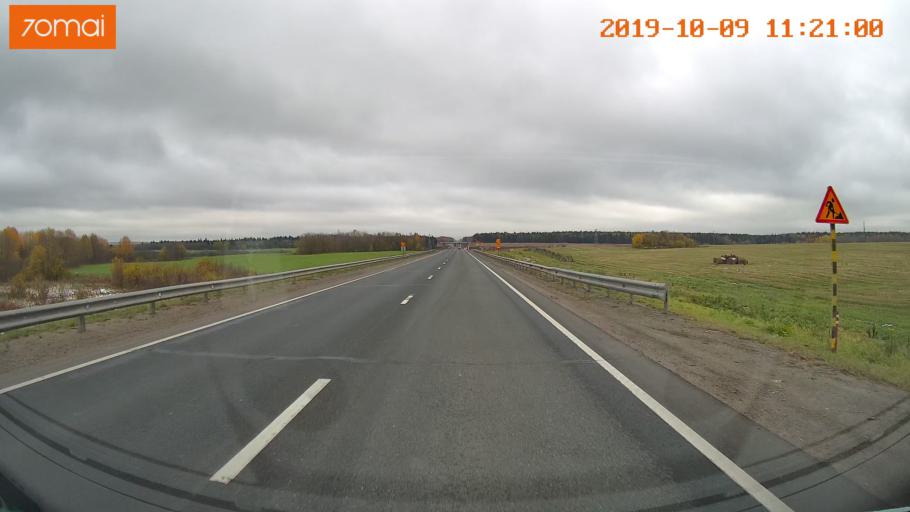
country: RU
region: Vologda
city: Vologda
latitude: 59.1434
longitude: 39.9453
